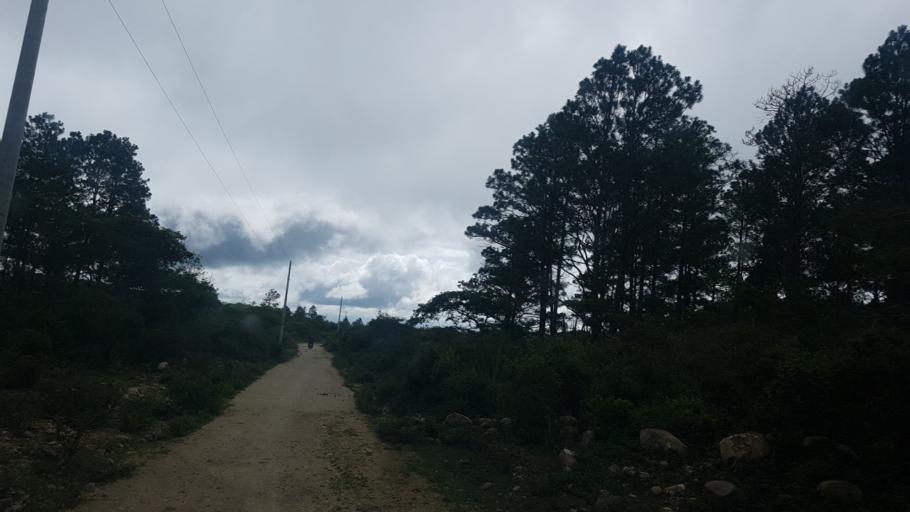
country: NI
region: Madriz
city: Totogalpa
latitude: 13.6137
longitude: -86.6076
